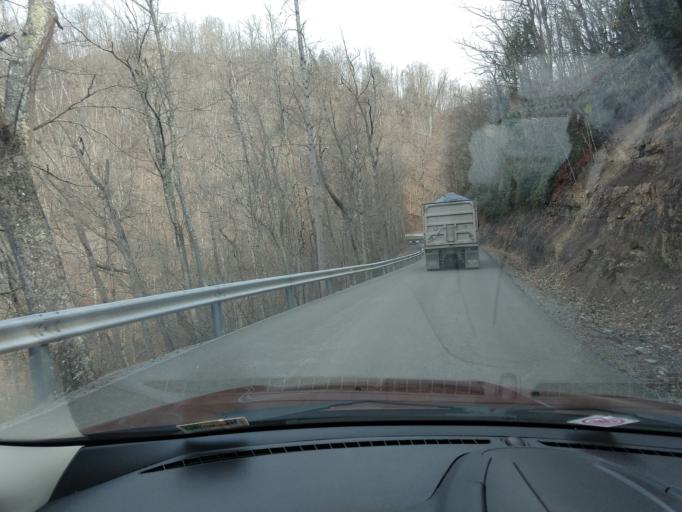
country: US
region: West Virginia
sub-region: Tucker County
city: Parsons
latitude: 39.0204
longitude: -79.5242
